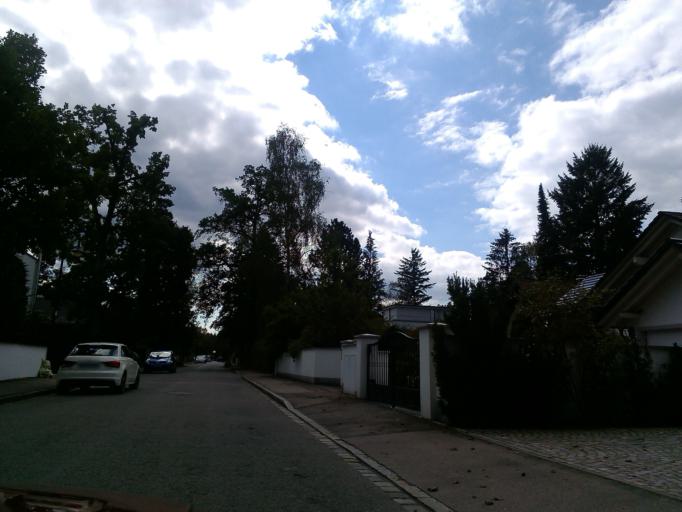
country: DE
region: Bavaria
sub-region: Upper Bavaria
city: Grafelfing
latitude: 48.1173
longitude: 11.4178
